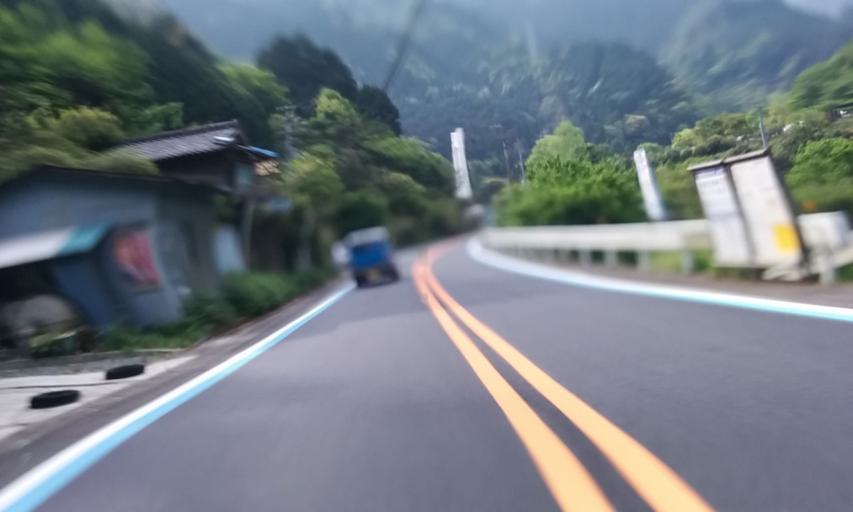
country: JP
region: Ehime
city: Niihama
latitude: 33.9052
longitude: 133.3092
